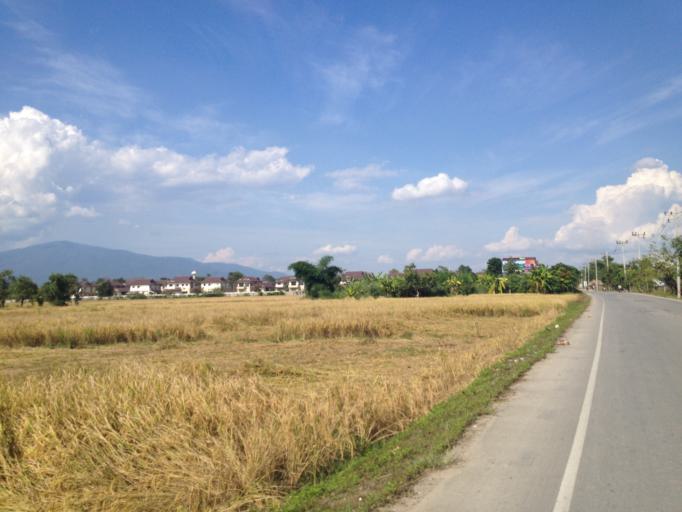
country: TH
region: Chiang Mai
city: Hang Dong
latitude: 18.6948
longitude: 98.9634
